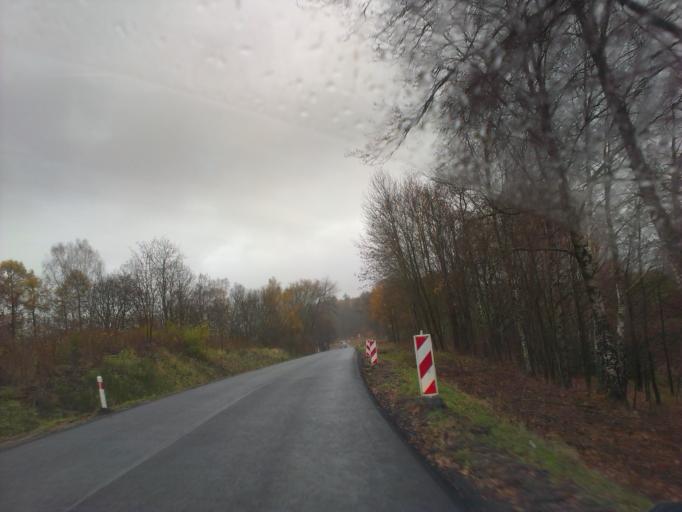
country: PL
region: West Pomeranian Voivodeship
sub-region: Powiat szczecinecki
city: Borne Sulinowo
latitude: 53.6186
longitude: 16.5396
